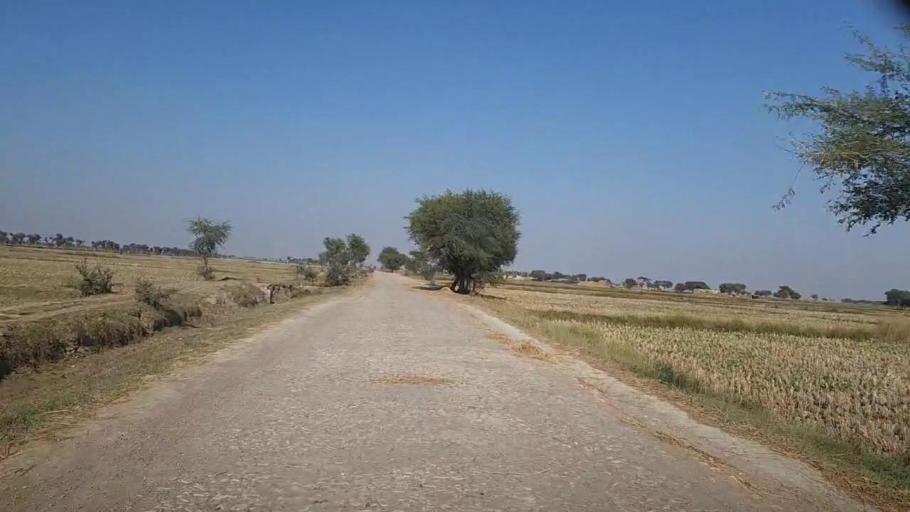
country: PK
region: Sindh
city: Thul
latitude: 28.3510
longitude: 68.7629
